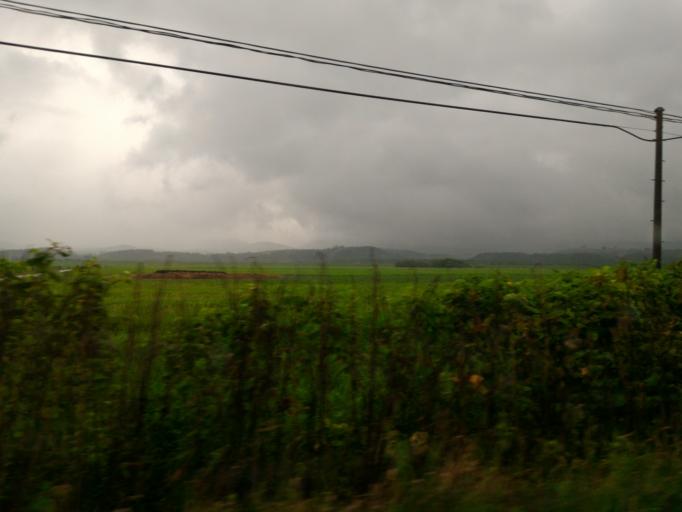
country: JP
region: Hokkaido
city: Makubetsu
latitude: 44.8281
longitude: 142.0618
